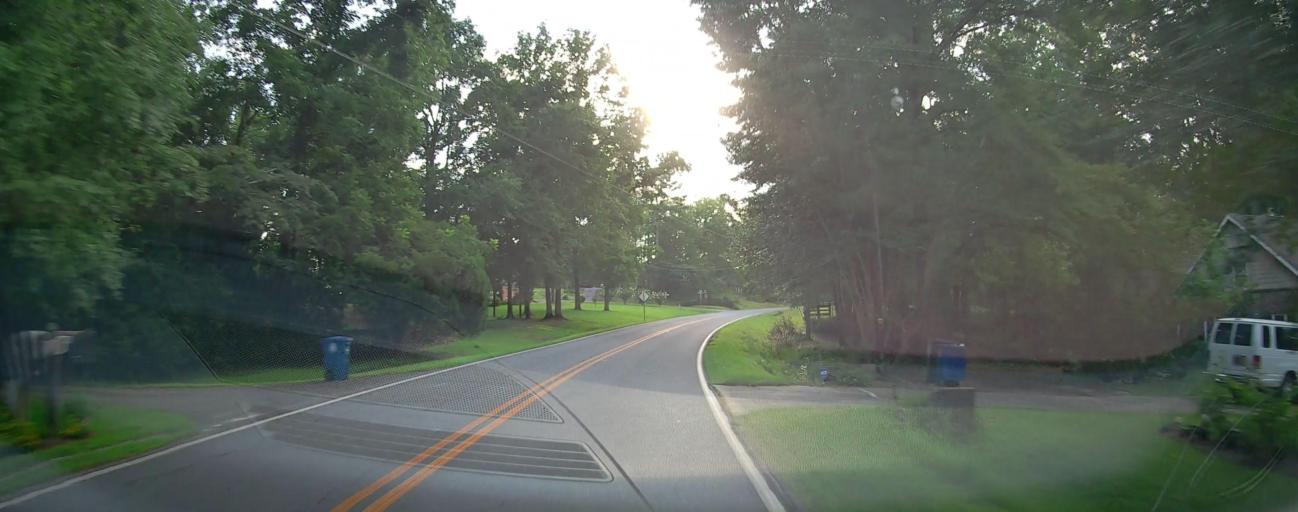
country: US
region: Georgia
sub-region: Peach County
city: Byron
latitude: 32.7167
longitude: -83.7524
